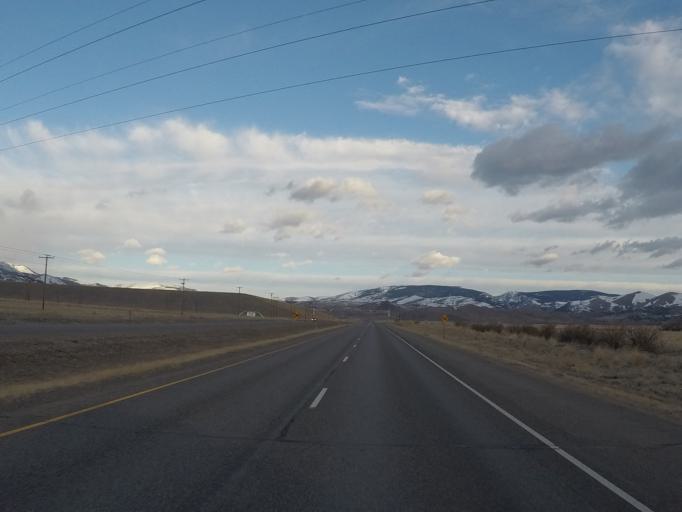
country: US
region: Montana
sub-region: Deer Lodge County
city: Anaconda
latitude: 46.1152
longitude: -112.8664
